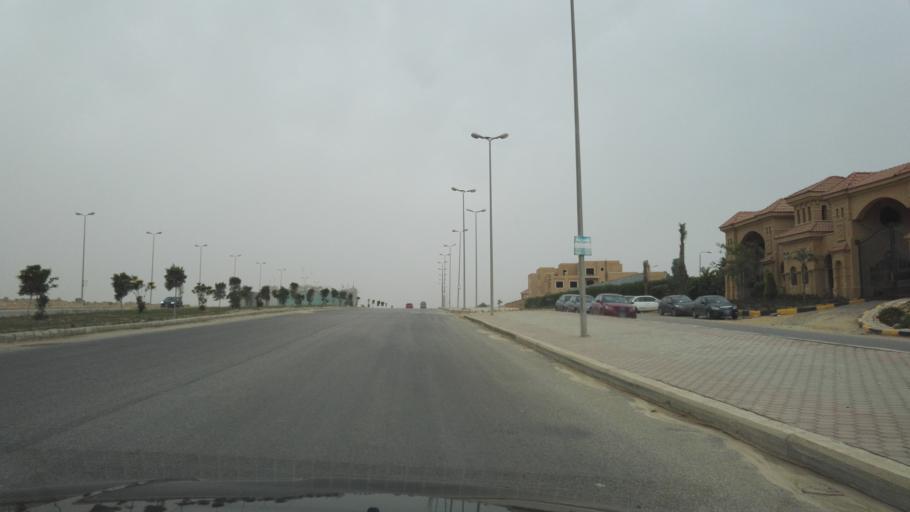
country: EG
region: Muhafazat al Qalyubiyah
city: Al Khankah
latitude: 30.0370
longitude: 31.5154
